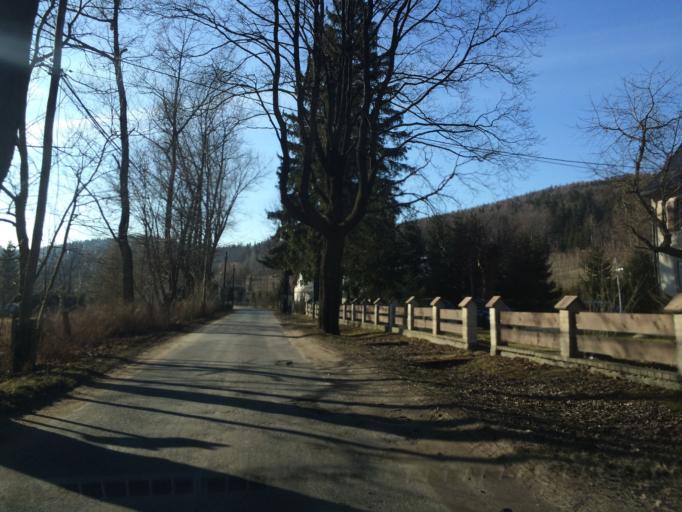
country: PL
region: Lower Silesian Voivodeship
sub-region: Powiat klodzki
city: Stronie Slaskie
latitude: 50.3095
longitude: 16.9171
